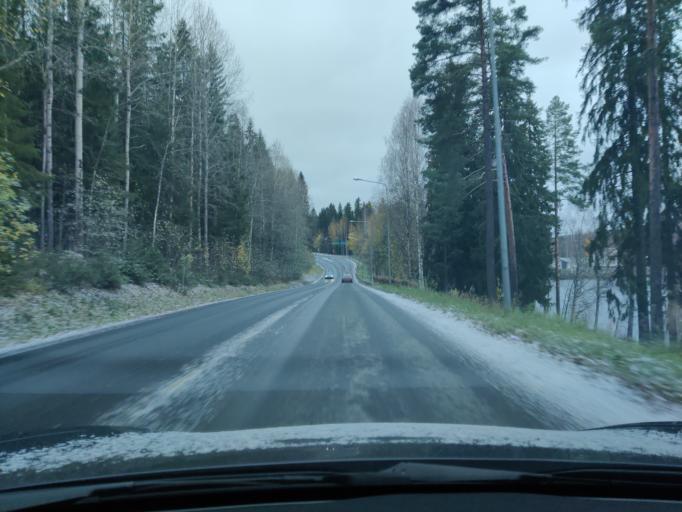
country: FI
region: Northern Savo
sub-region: Kuopio
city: Kuopio
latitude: 62.8430
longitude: 27.6315
